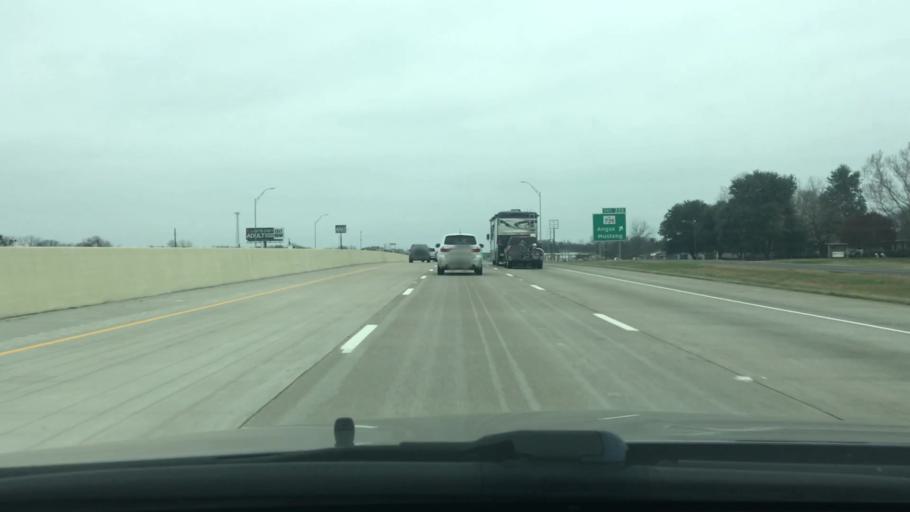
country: US
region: Texas
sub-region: Navarro County
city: Corsicana
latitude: 32.0139
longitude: -96.4363
